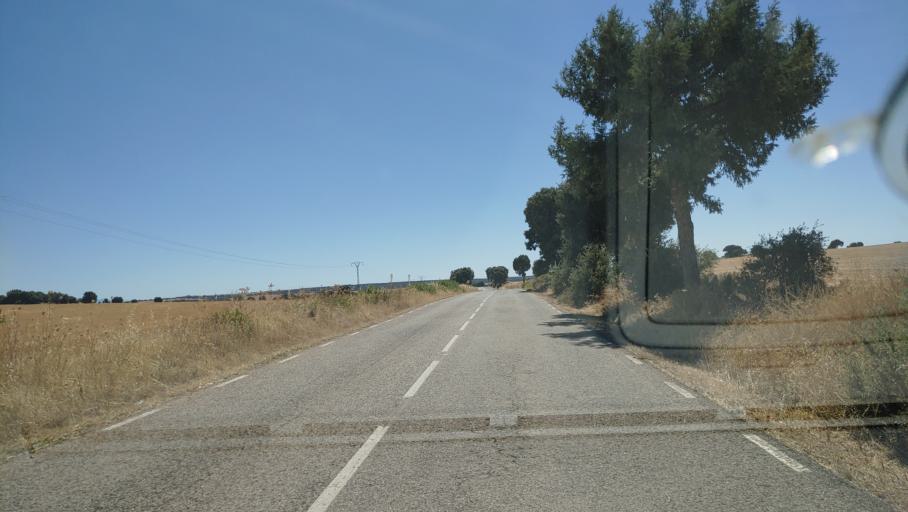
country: ES
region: Castille-La Mancha
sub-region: Provincia de Albacete
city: Ossa de Montiel
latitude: 38.9142
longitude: -2.7588
